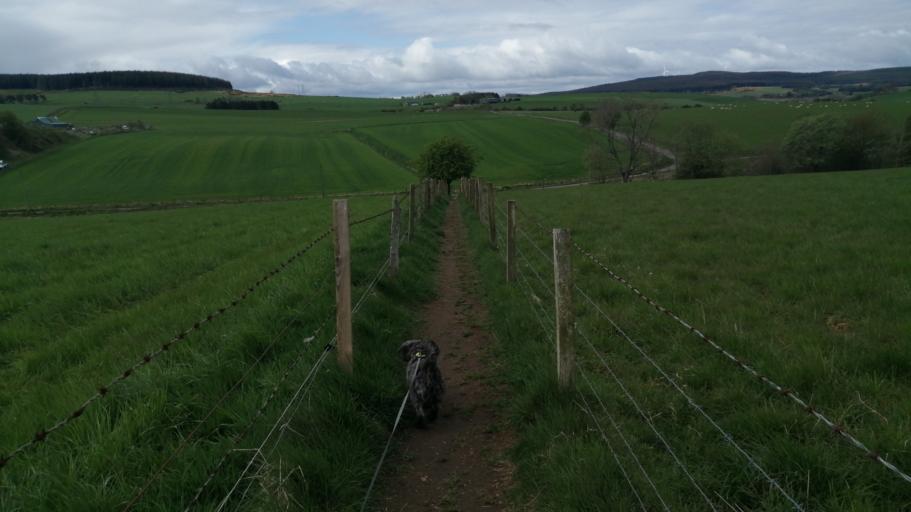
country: GB
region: Scotland
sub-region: Moray
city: Keith
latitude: 57.5313
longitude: -2.9606
